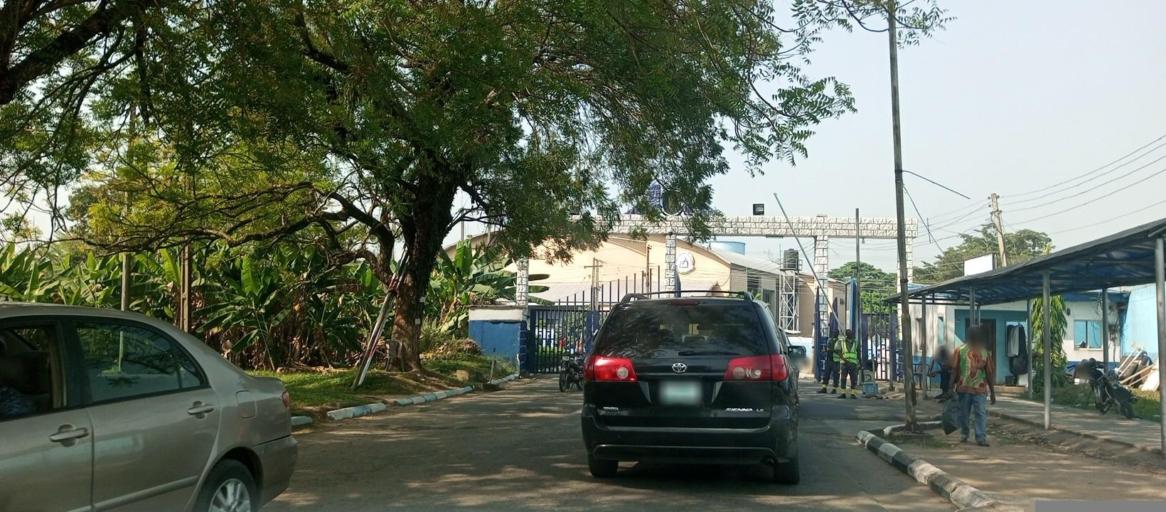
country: NG
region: Rivers
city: Emuoha
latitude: 4.9018
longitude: 6.9068
